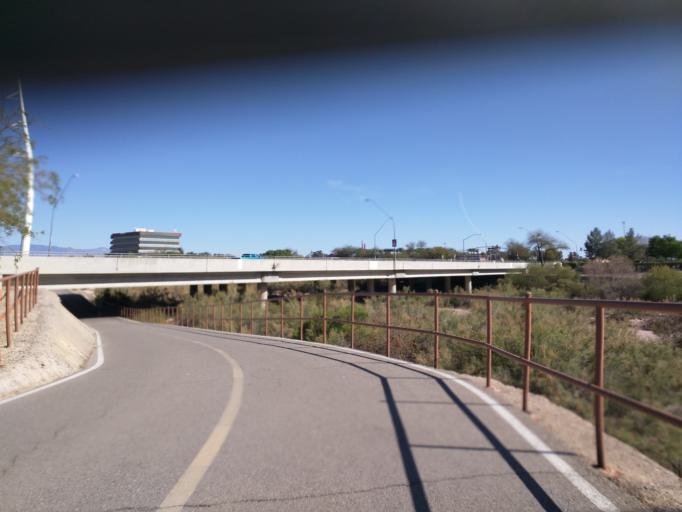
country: US
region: Arizona
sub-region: Pima County
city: Flowing Wells
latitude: 32.2905
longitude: -110.9707
